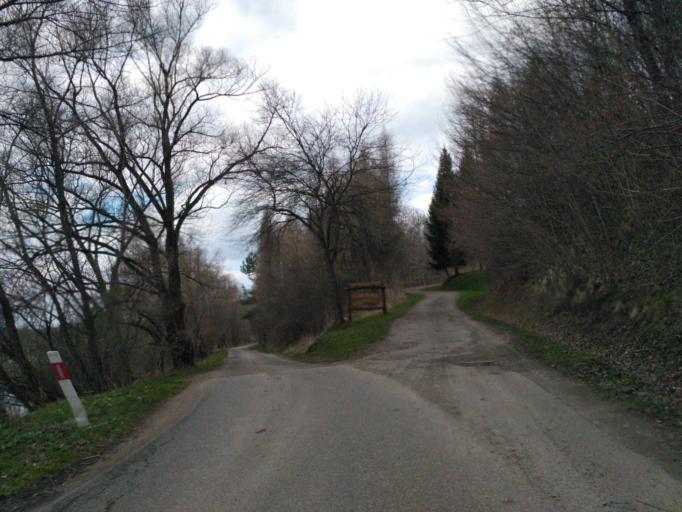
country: PL
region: Subcarpathian Voivodeship
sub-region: Powiat sanocki
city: Tyrawa Woloska
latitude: 49.6614
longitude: 22.2983
